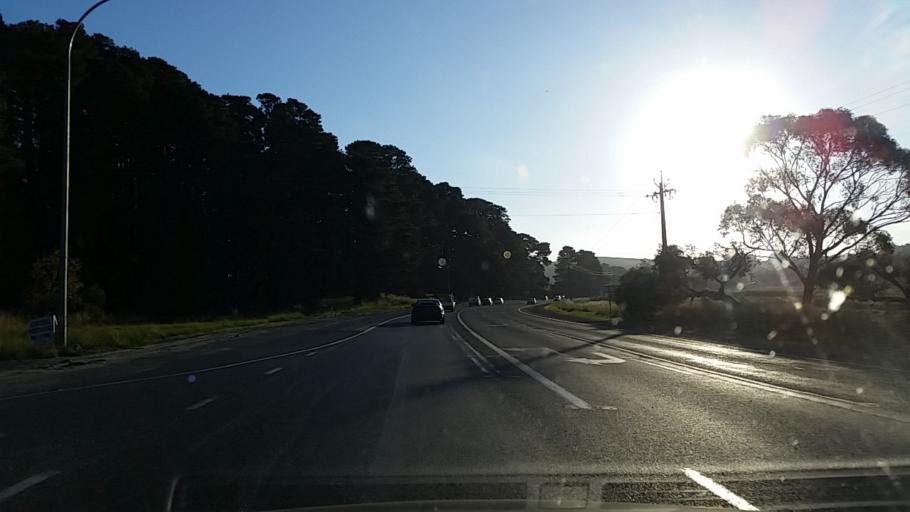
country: AU
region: South Australia
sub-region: Alexandrina
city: Mount Compass
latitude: -35.3435
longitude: 138.6056
